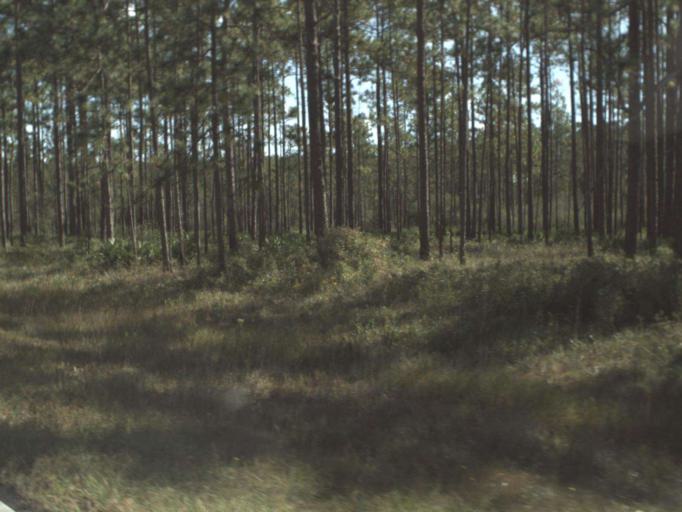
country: US
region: Florida
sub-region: Liberty County
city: Bristol
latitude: 30.1923
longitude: -84.9241
